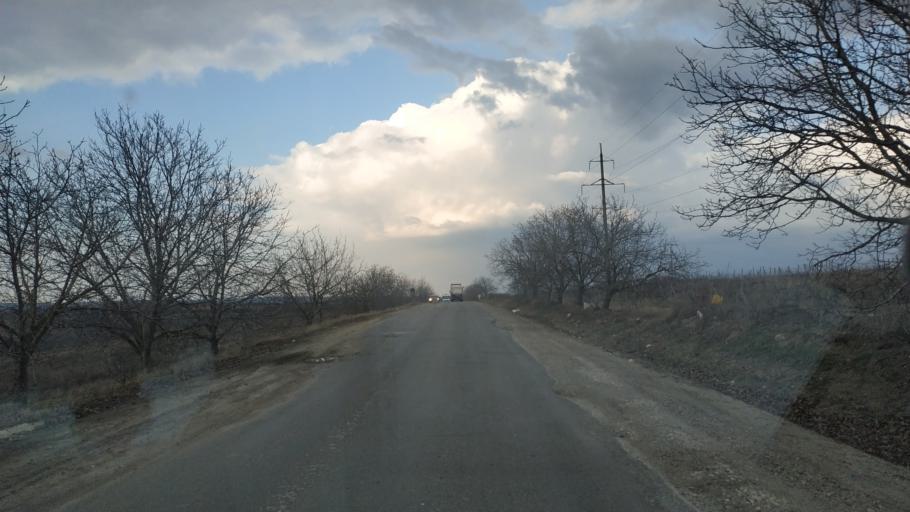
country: MD
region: Anenii Noi
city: Anenii Noi
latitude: 46.9627
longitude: 29.2846
